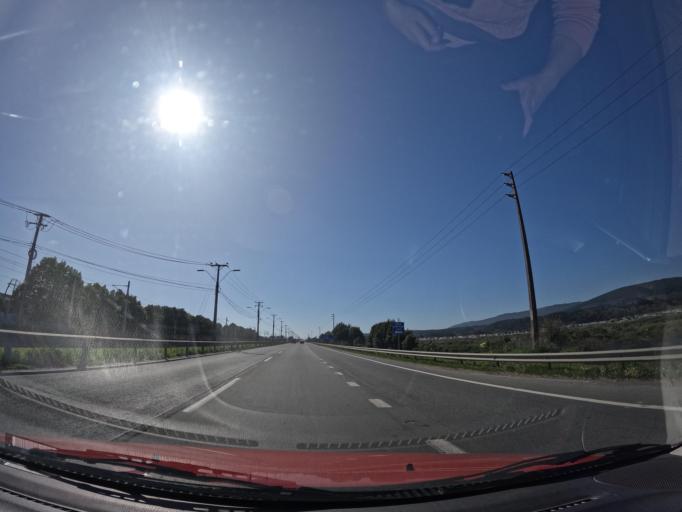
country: CL
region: Biobio
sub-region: Provincia de Concepcion
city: Coronel
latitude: -36.9633
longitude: -73.1584
